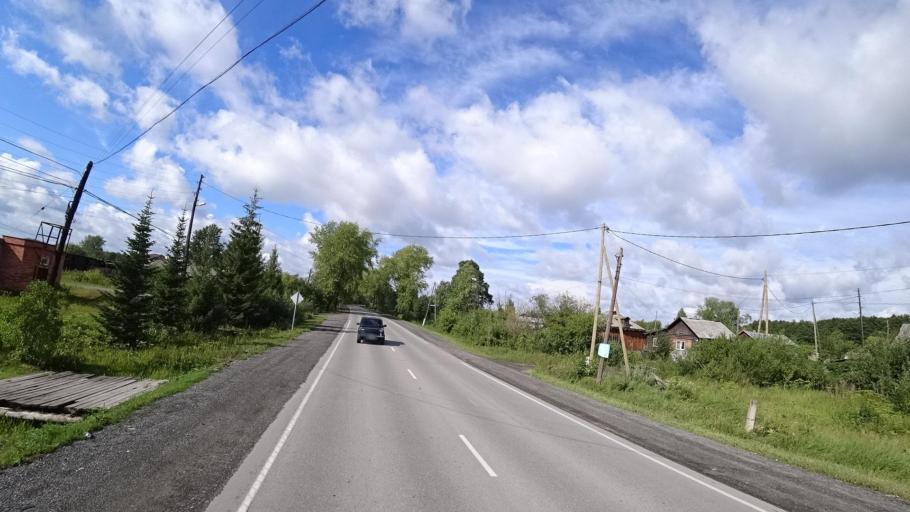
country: RU
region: Sverdlovsk
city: Kamyshlov
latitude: 56.8320
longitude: 62.6958
